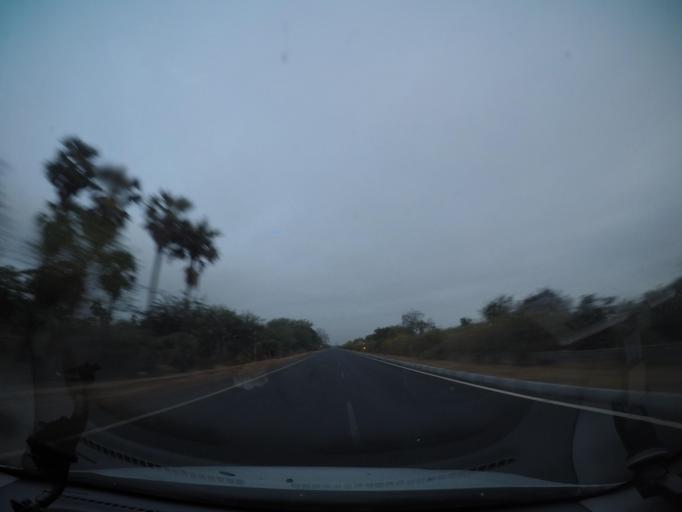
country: IN
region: Andhra Pradesh
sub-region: West Godavari
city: Tadepallegudem
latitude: 16.8102
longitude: 81.3401
